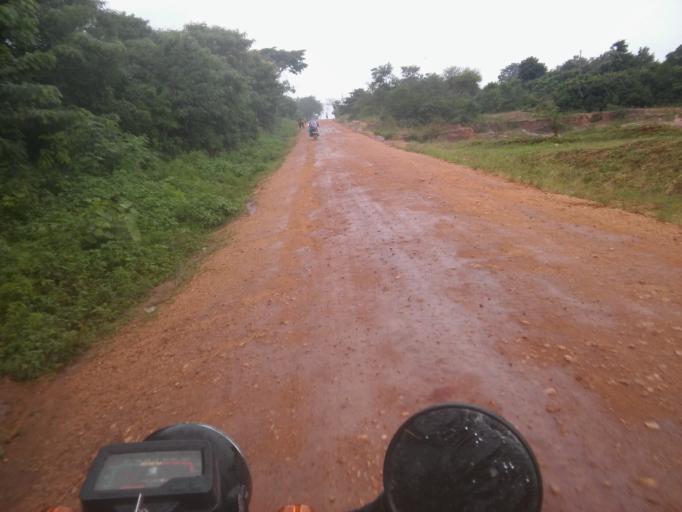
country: UG
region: Eastern Region
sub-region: Mbale District
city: Mbale
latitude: 0.9833
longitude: 34.2017
